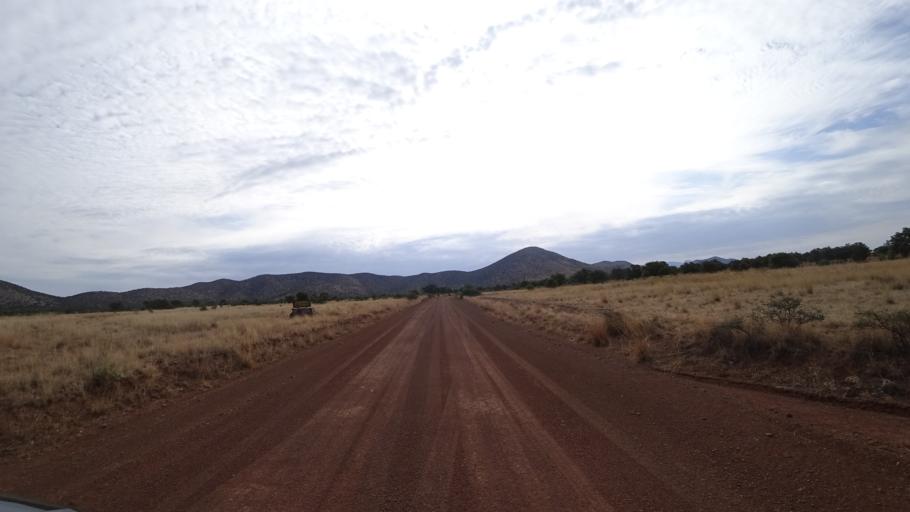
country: MX
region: Sonora
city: Santa Cruz
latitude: 31.4819
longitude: -110.5682
